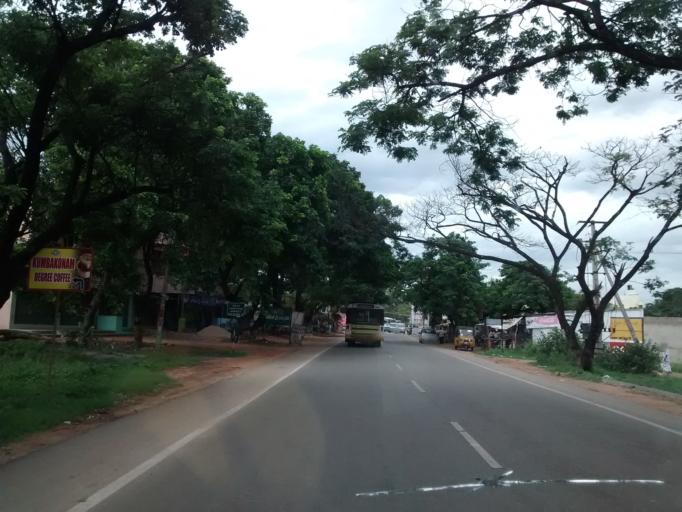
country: IN
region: Andhra Pradesh
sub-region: Chittoor
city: Narasingapuram
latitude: 13.6134
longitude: 79.3618
